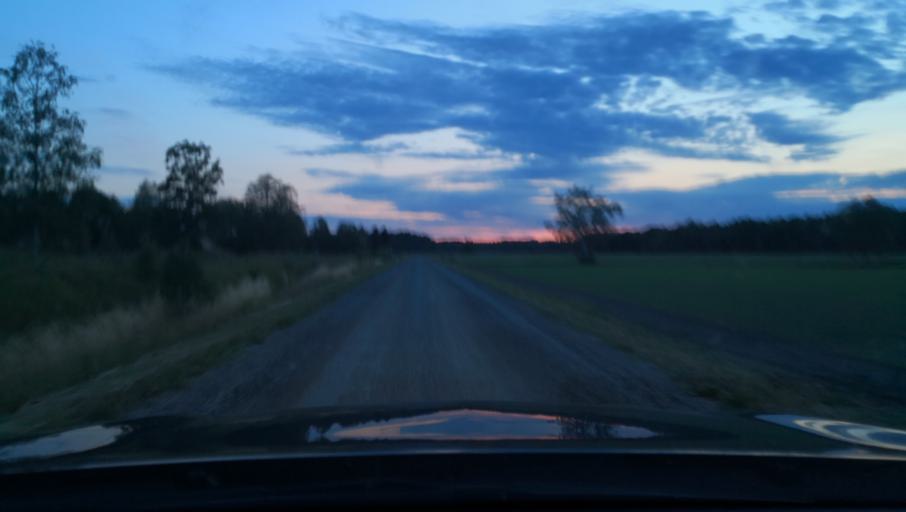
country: SE
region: Uppsala
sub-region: Heby Kommun
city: OEstervala
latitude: 60.0120
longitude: 17.3169
